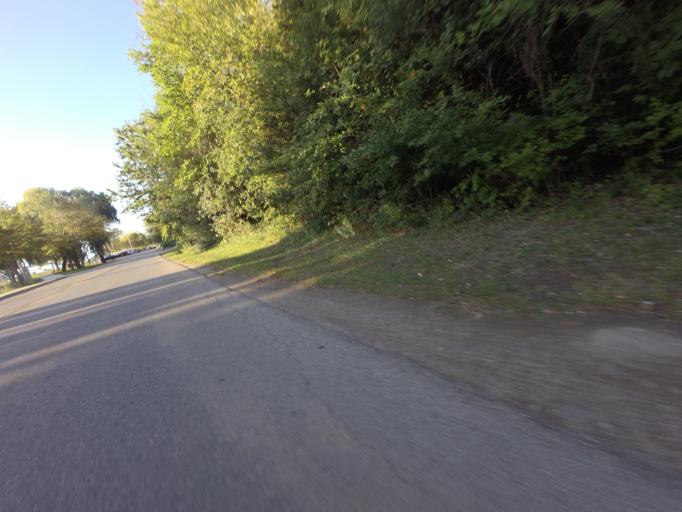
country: CA
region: Ontario
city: Goderich
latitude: 43.7397
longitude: -81.7259
